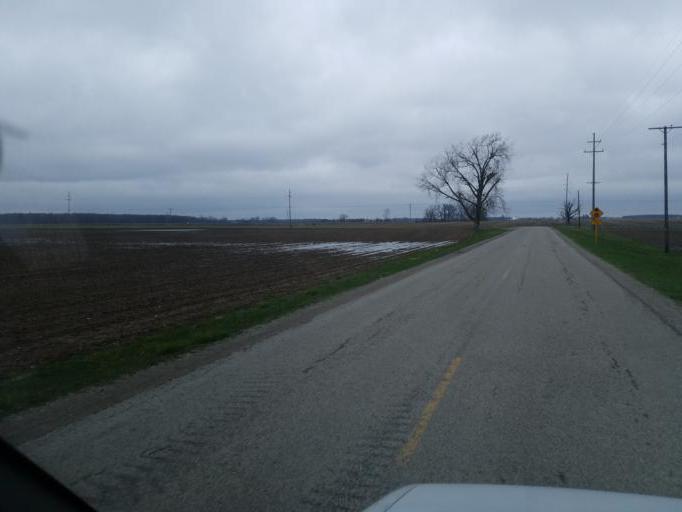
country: US
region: Ohio
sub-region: Marion County
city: Marion
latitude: 40.6719
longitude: -83.0732
